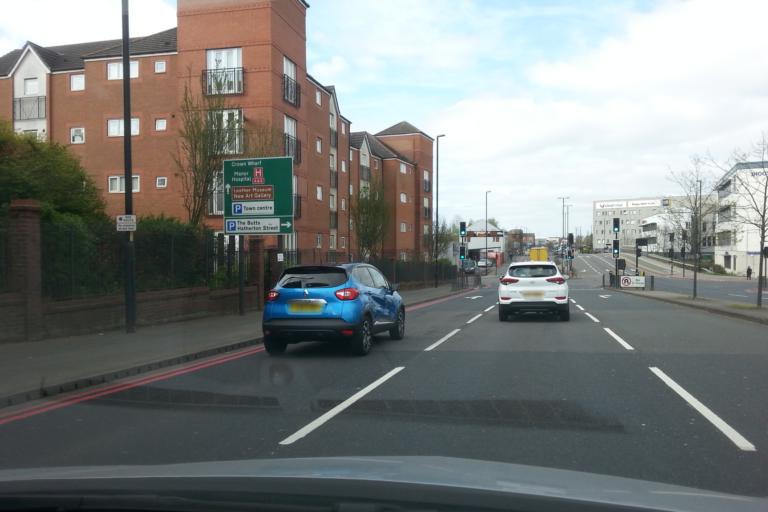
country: GB
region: England
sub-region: Walsall
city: Walsall
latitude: 52.5888
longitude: -1.9783
